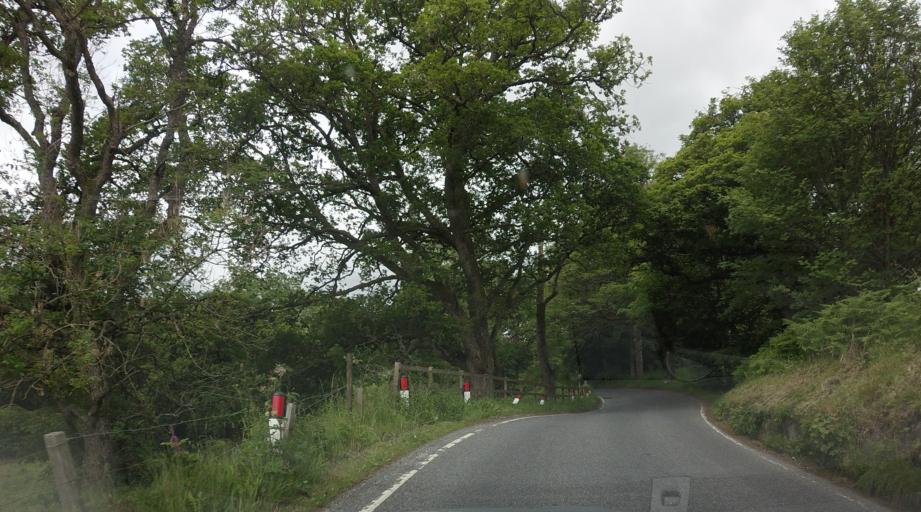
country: GB
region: Scotland
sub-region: Perth and Kinross
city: Pitlochry
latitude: 56.7262
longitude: -3.7852
